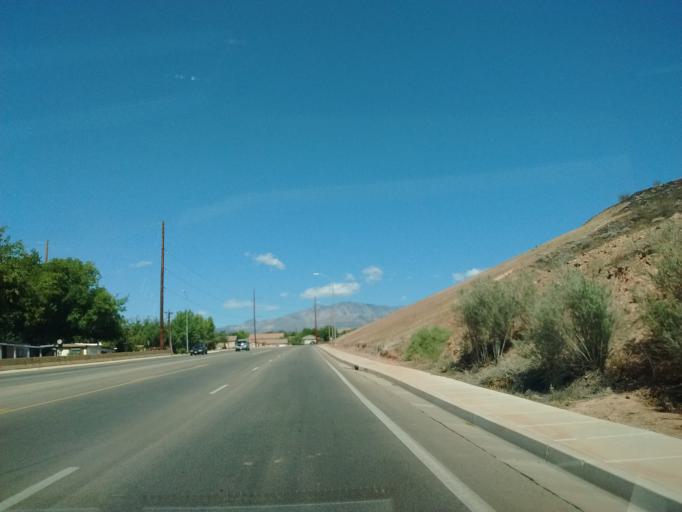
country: US
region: Utah
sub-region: Washington County
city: Washington
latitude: 37.1241
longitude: -113.5052
